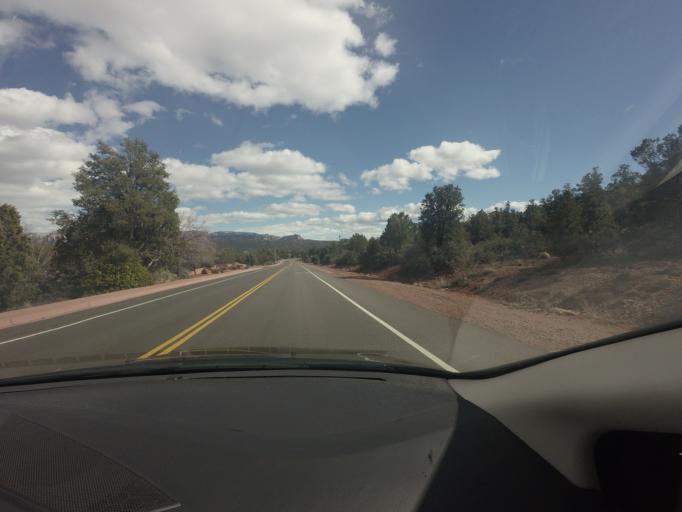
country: US
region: Arizona
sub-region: Yavapai County
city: West Sedona
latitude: 34.8678
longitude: -111.8208
